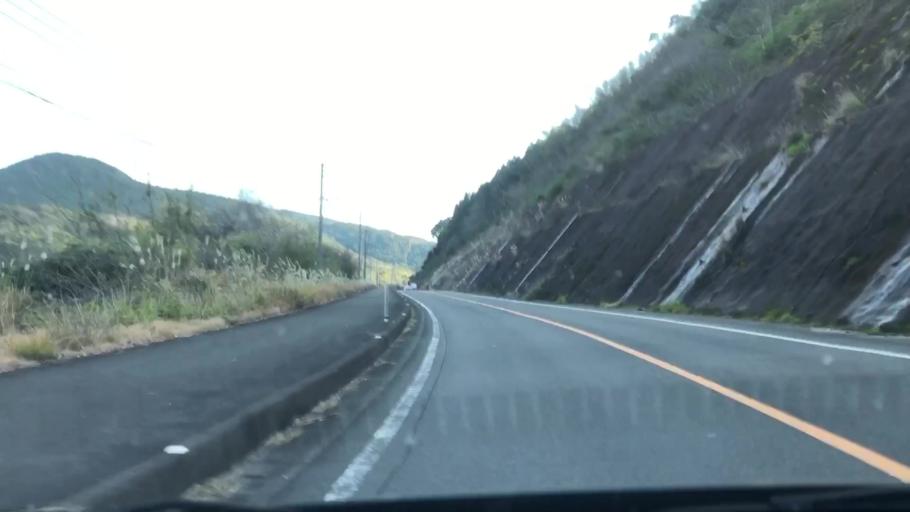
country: JP
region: Kagoshima
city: Satsumasendai
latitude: 31.8569
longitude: 130.3163
